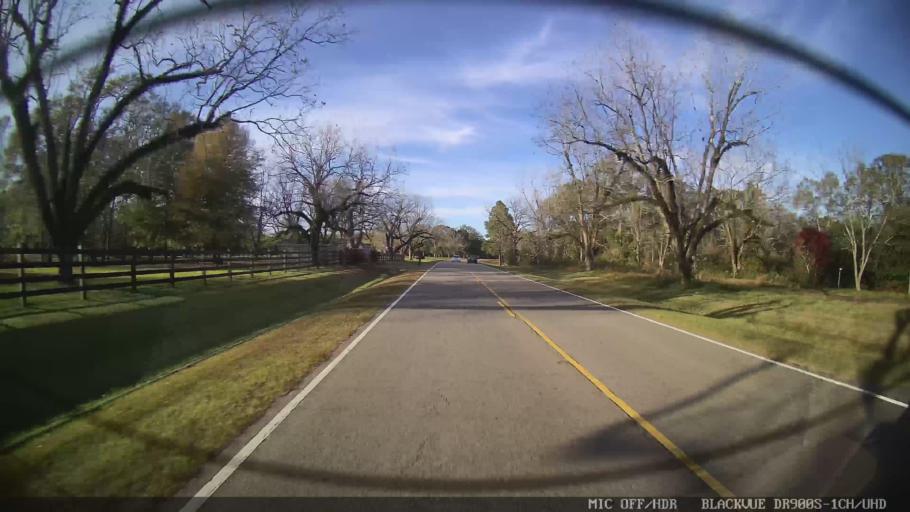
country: US
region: Mississippi
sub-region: Forrest County
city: Hattiesburg
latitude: 31.2015
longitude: -89.2927
